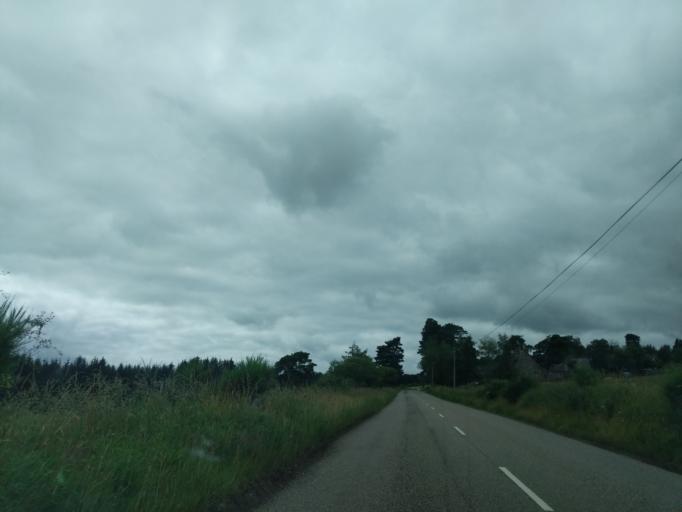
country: GB
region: Scotland
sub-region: Moray
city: Rothes
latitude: 57.4873
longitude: -3.2473
